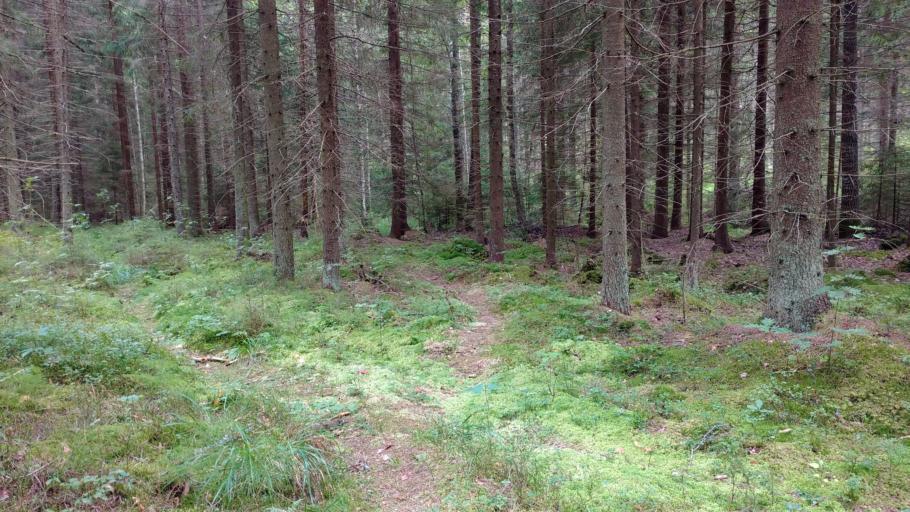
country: FI
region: Varsinais-Suomi
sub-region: Salo
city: Salo
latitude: 60.3572
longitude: 23.1619
